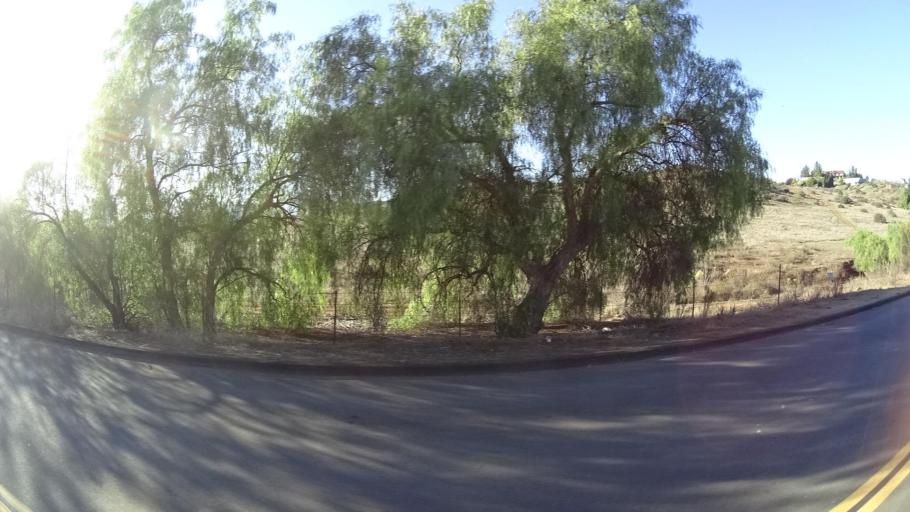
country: US
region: California
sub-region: San Diego County
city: Jamul
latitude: 32.7070
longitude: -116.8734
